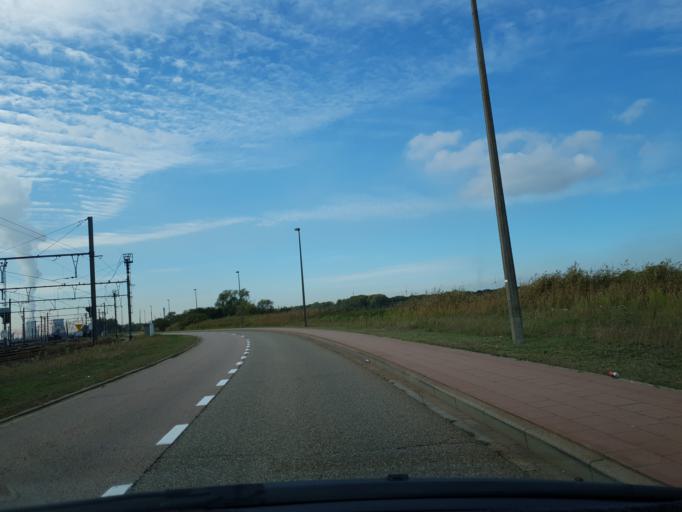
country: BE
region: Flanders
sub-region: Provincie Antwerpen
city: Stabroek
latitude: 51.3351
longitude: 4.3389
